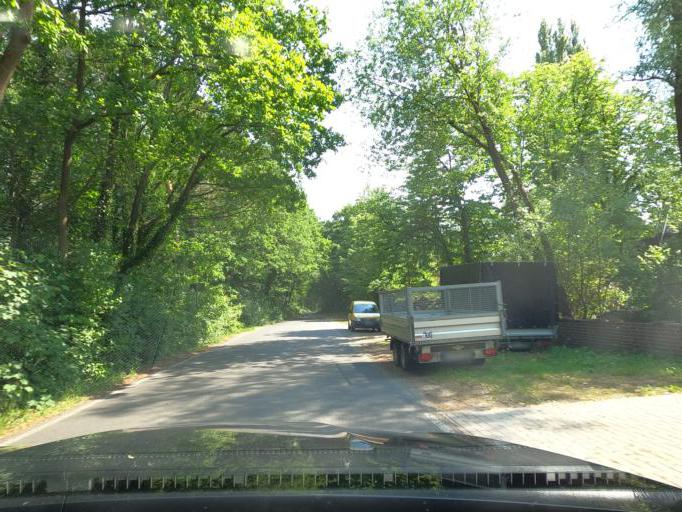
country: DE
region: Lower Saxony
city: Isernhagen Farster Bauerschaft
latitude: 52.4032
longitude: 9.8563
